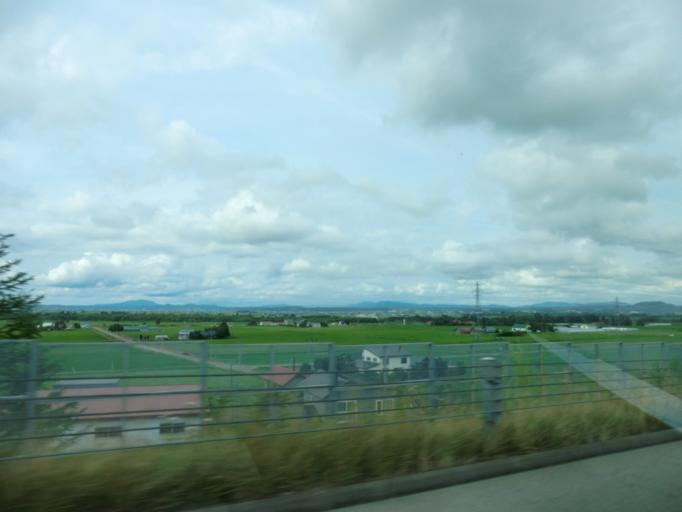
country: JP
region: Hokkaido
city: Fukagawa
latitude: 43.6621
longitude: 142.0136
